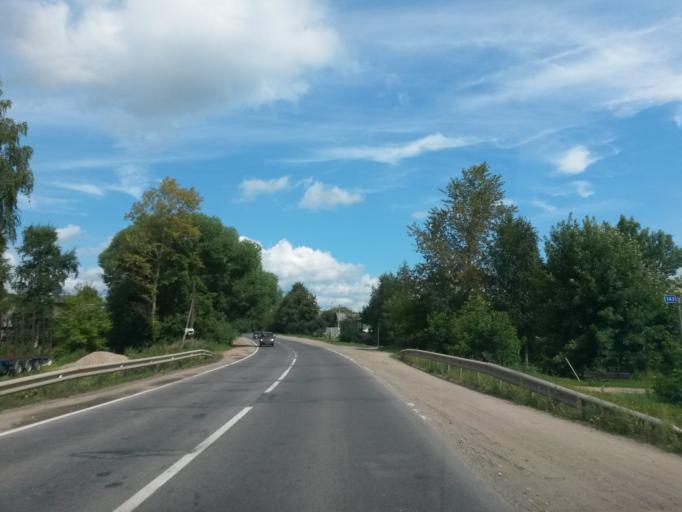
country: RU
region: Jaroslavl
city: Pereslavl'-Zalesskiy
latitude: 56.7646
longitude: 38.8725
